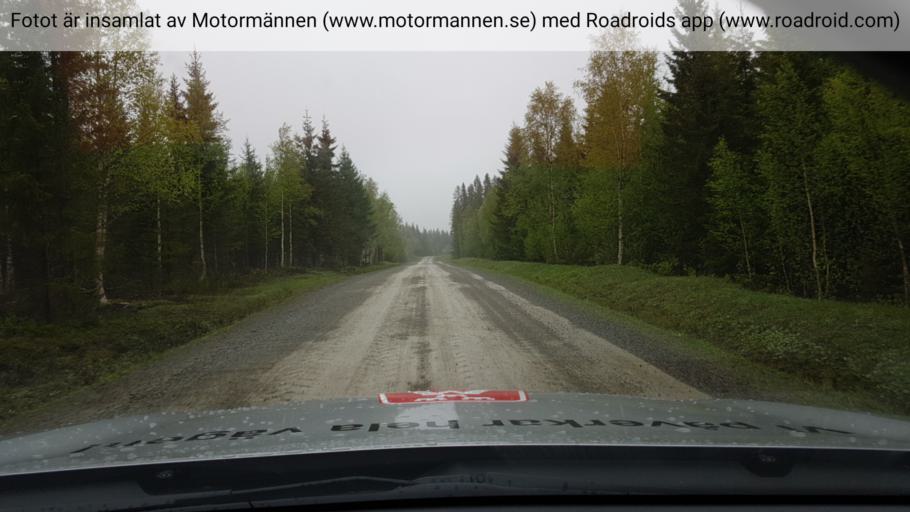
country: SE
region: Jaemtland
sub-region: Bergs Kommun
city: Hoverberg
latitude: 62.9713
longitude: 14.2237
